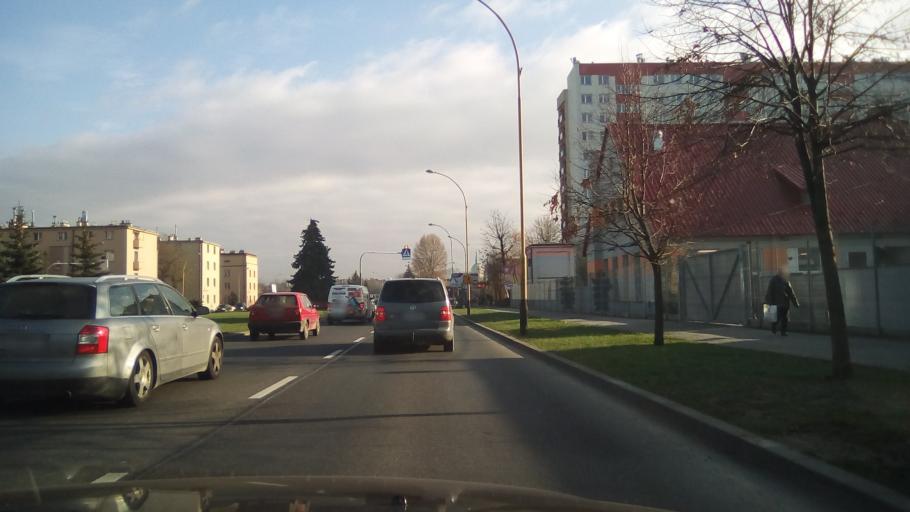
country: PL
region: Subcarpathian Voivodeship
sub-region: Rzeszow
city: Rzeszow
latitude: 50.0443
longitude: 21.9850
